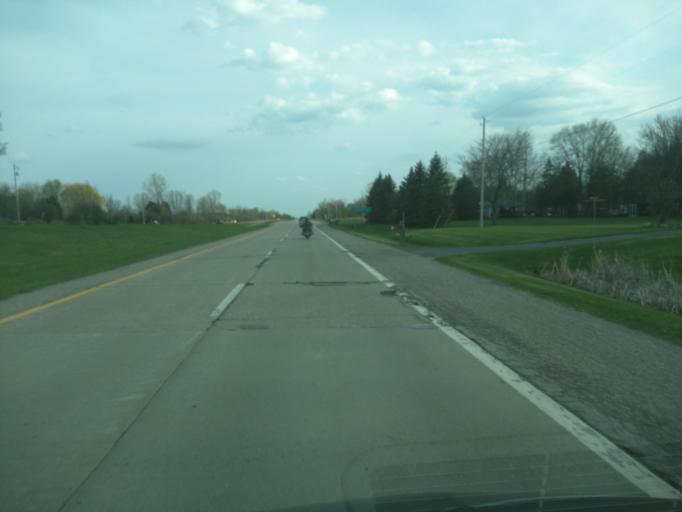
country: US
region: Michigan
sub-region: Eaton County
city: Dimondale
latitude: 42.5916
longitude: -84.6224
